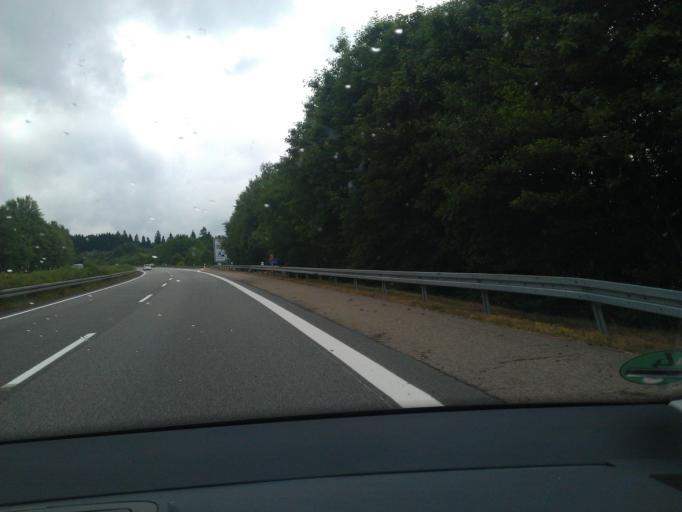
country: DE
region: Rheinland-Pfalz
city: Achtelsbach
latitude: 49.5954
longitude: 7.0488
